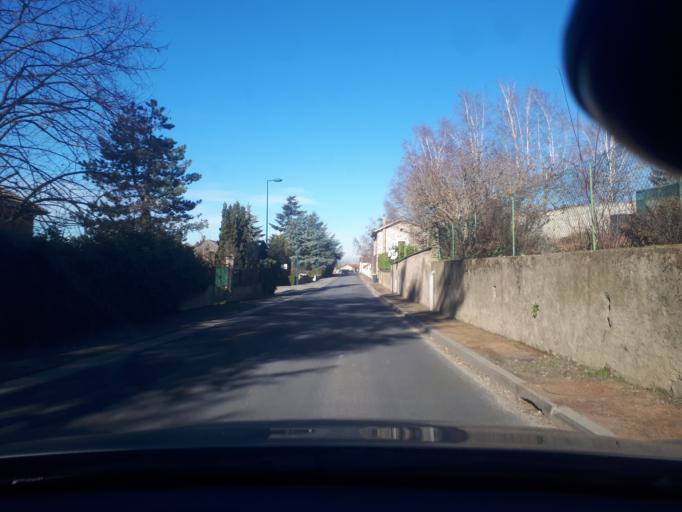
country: FR
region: Rhone-Alpes
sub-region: Departement de la Loire
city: Bellegarde-en-Forez
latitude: 45.6364
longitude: 4.3010
